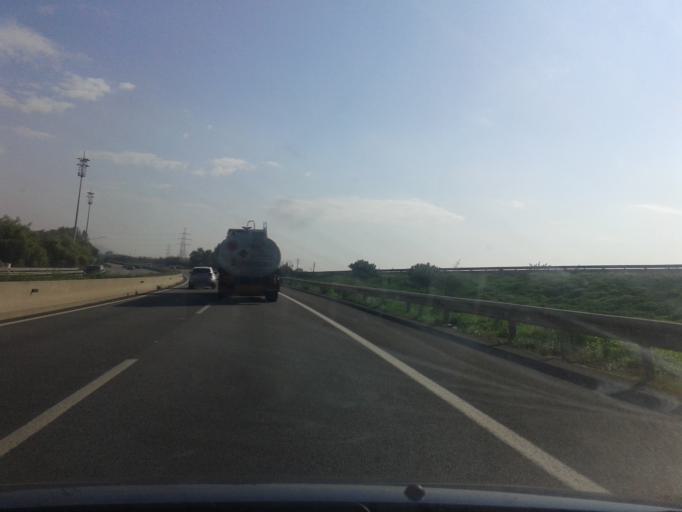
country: ES
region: Catalonia
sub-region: Provincia de Barcelona
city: Cornella de Llobregat
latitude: 41.3328
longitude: 2.0708
